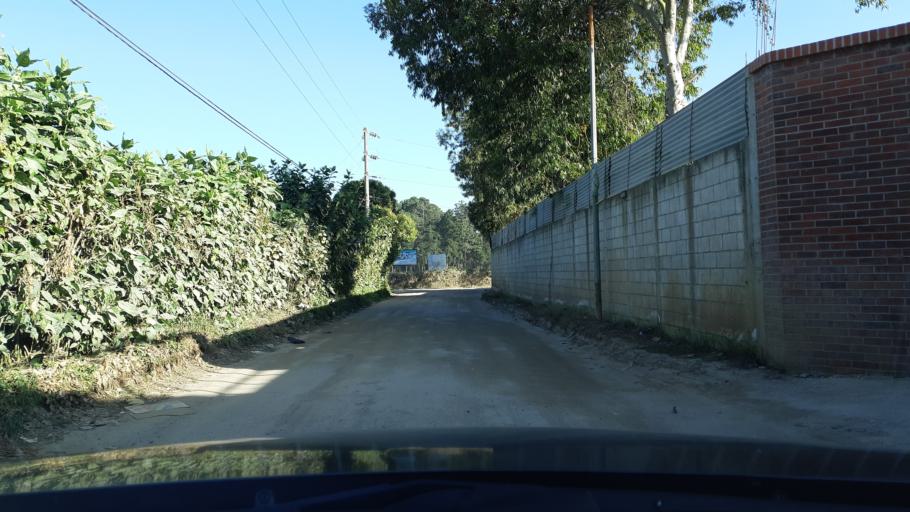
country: GT
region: Chimaltenango
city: El Tejar
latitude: 14.6368
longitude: -90.8006
